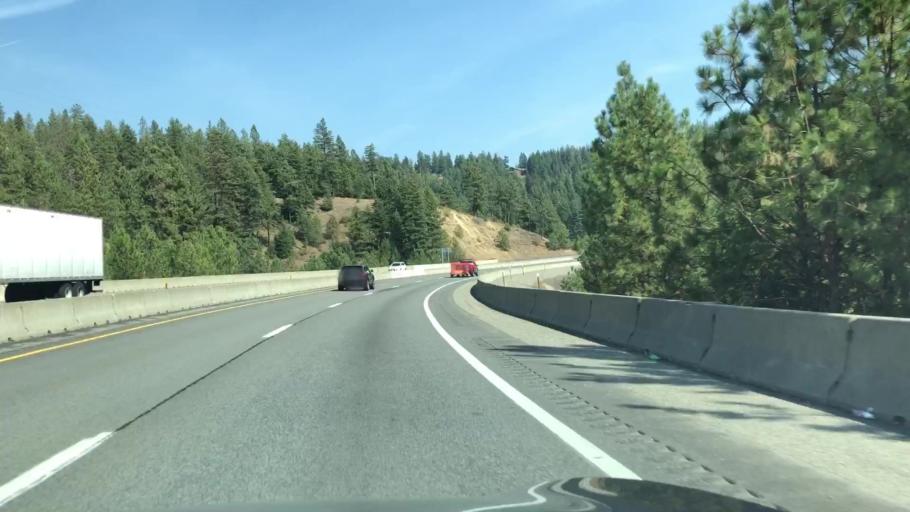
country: US
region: Idaho
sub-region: Kootenai County
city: Coeur d'Alene
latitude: 47.6627
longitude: -116.7340
